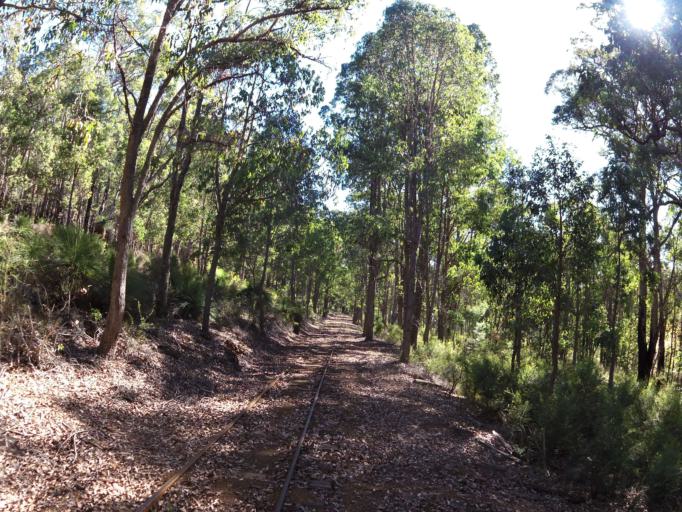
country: AU
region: Western Australia
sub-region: Waroona
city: Waroona
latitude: -32.7104
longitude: 116.0831
